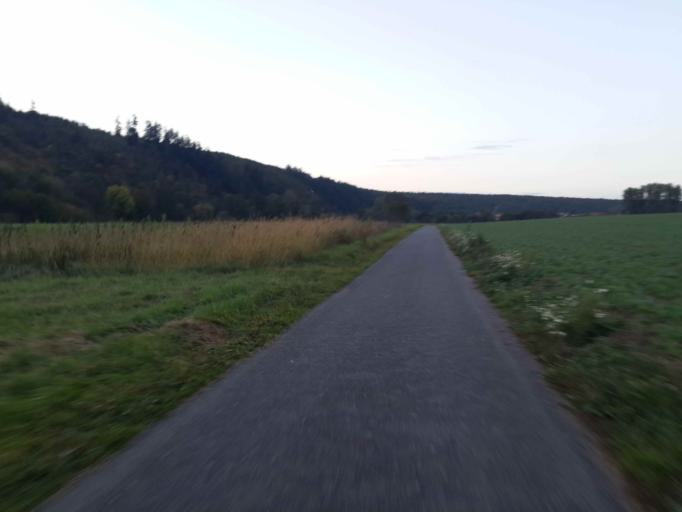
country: DE
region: Bavaria
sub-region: Regierungsbezirk Unterfranken
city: Kreuzwertheim
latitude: 49.7638
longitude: 9.5607
